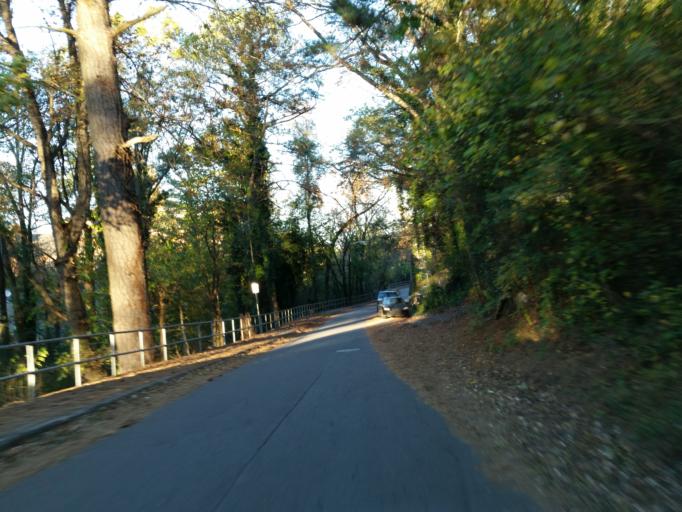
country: US
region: Georgia
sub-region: Cobb County
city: Marietta
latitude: 33.9560
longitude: -84.5396
